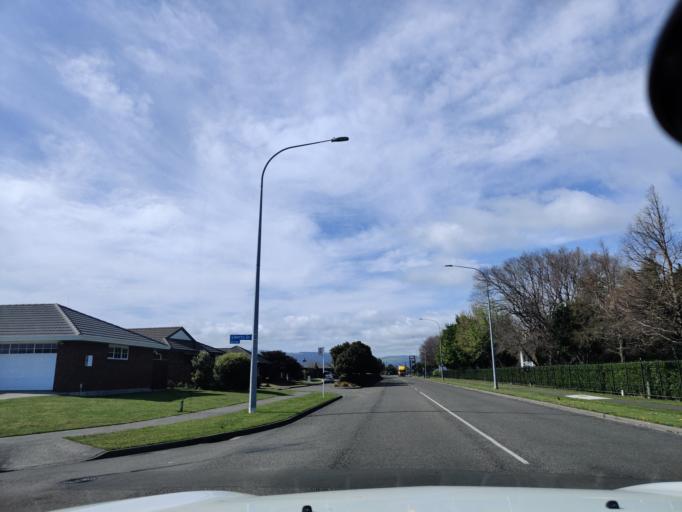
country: NZ
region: Manawatu-Wanganui
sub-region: Palmerston North City
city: Palmerston North
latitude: -40.3317
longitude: 175.6532
